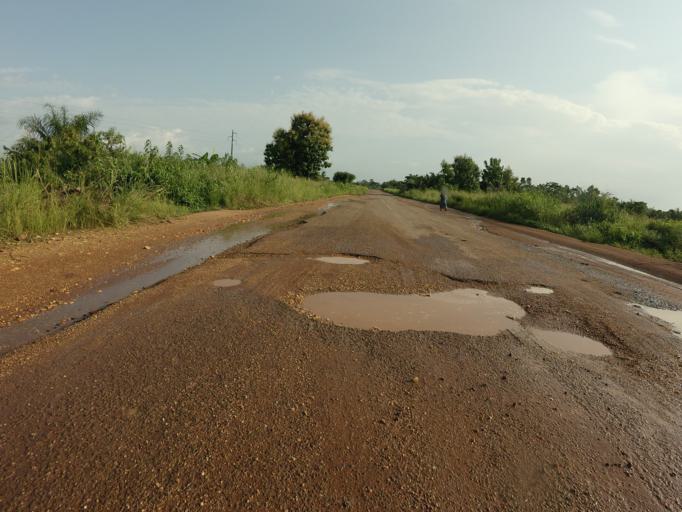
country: GH
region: Volta
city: Hohoe
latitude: 7.0762
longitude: 0.4379
